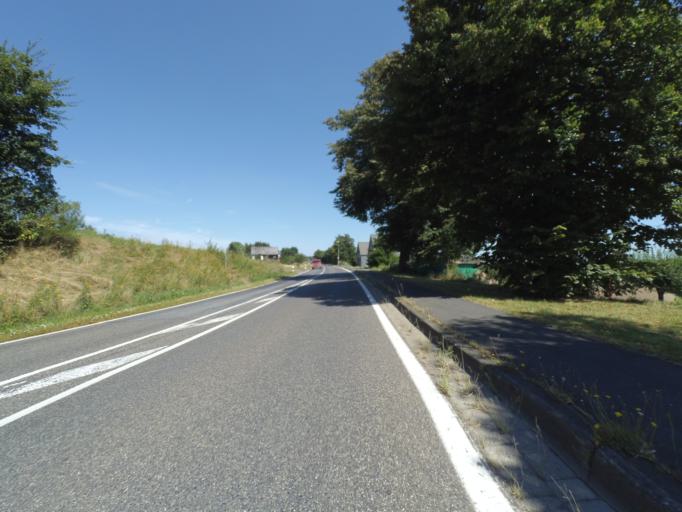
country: DE
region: Rheinland-Pfalz
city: Mullenbach
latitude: 50.2258
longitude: 7.0718
